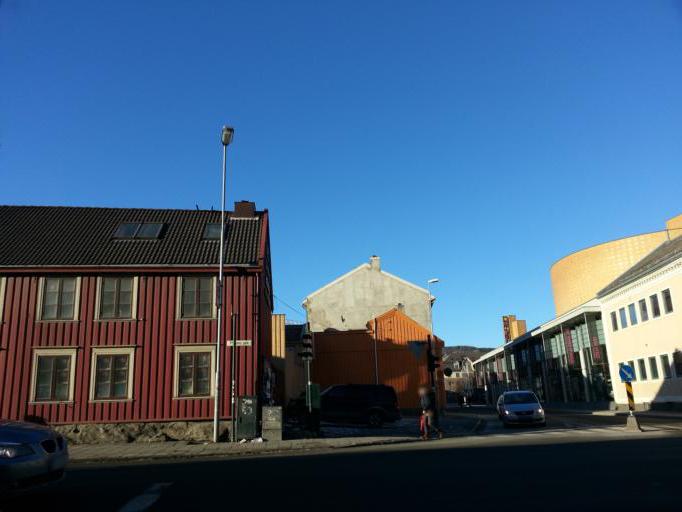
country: NO
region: Sor-Trondelag
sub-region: Trondheim
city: Trondheim
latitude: 63.4289
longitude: 10.3927
